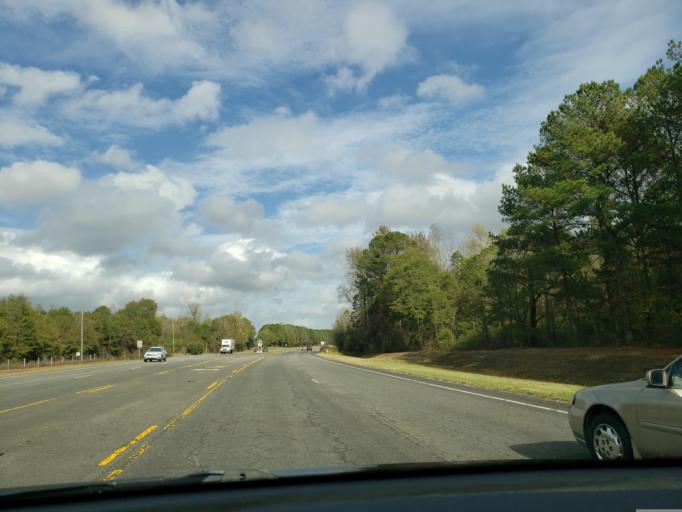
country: US
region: North Carolina
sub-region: Duplin County
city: Kenansville
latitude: 34.9242
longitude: -78.0166
